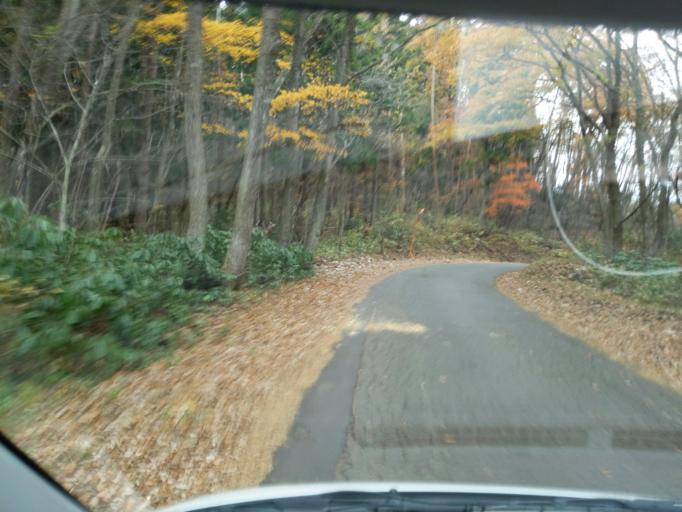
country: JP
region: Iwate
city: Ichinoseki
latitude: 38.9809
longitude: 141.0023
